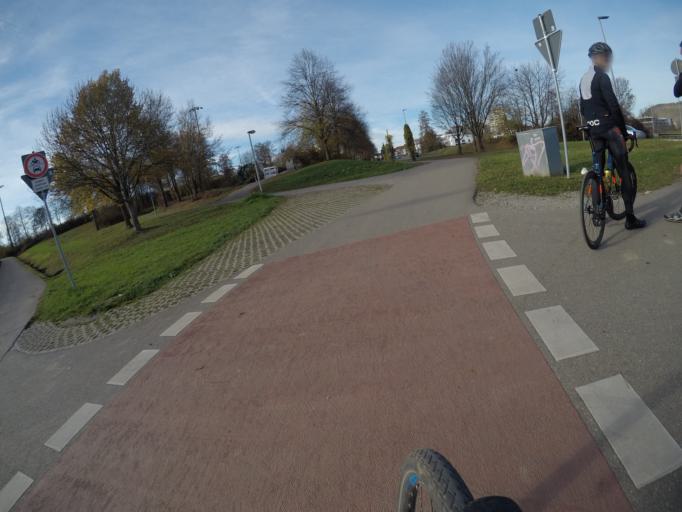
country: DE
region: Baden-Wuerttemberg
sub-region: Regierungsbezirk Stuttgart
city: Weinstadt-Endersbach
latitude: 48.8078
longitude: 9.3779
